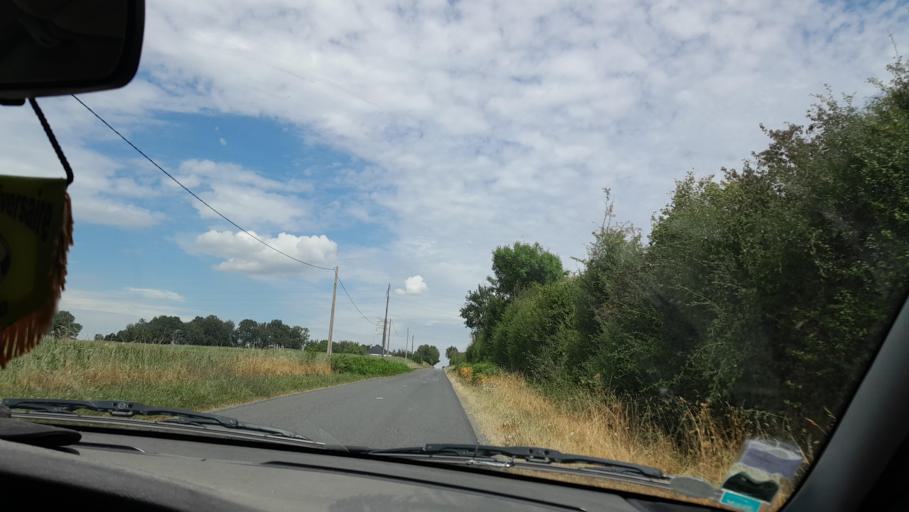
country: FR
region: Pays de la Loire
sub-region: Departement de la Mayenne
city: Saint-Pierre-la-Cour
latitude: 48.1226
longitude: -1.0250
